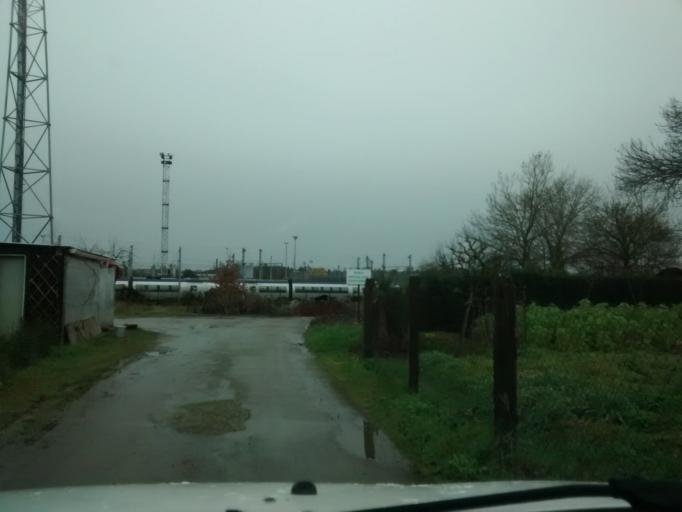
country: FR
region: Brittany
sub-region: Departement d'Ille-et-Vilaine
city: Chantepie
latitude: 48.1059
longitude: -1.6330
